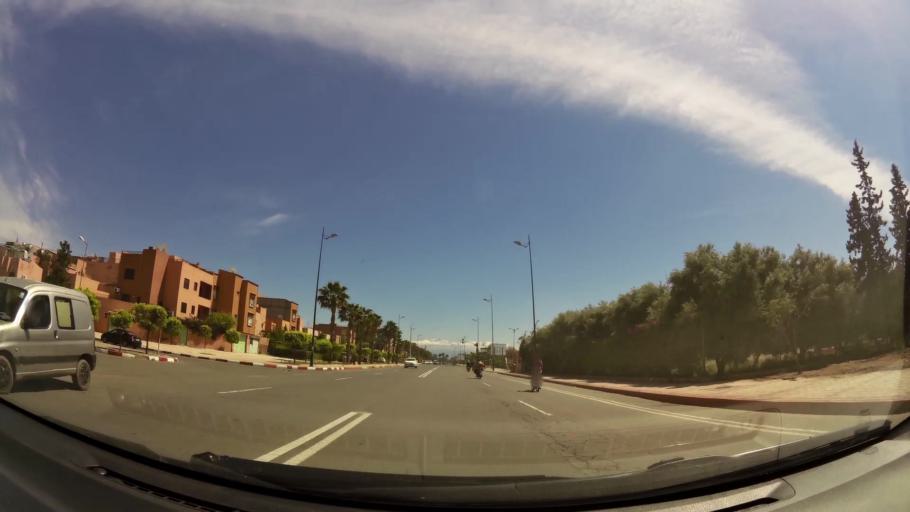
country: MA
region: Marrakech-Tensift-Al Haouz
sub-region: Marrakech
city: Marrakesh
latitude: 31.6052
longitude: -7.9723
